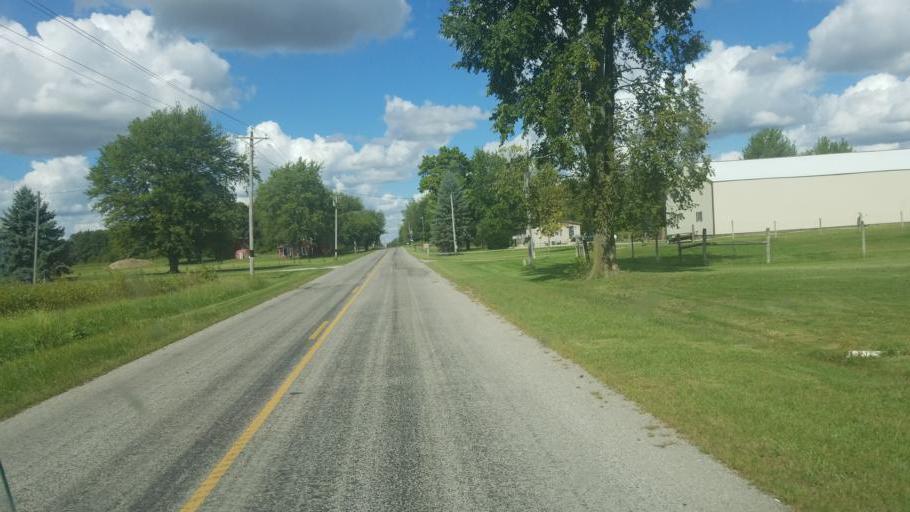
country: US
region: Ohio
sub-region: Champaign County
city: North Lewisburg
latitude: 40.3665
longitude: -83.5110
